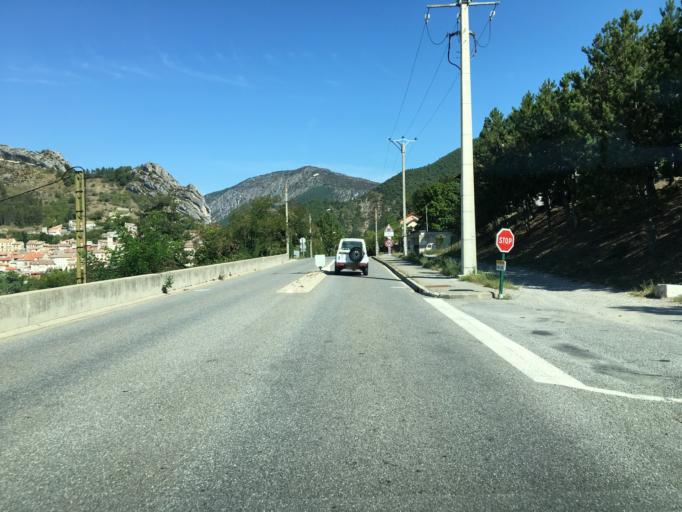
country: FR
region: Provence-Alpes-Cote d'Azur
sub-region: Departement des Hautes-Alpes
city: Serres
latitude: 44.4244
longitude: 5.7189
